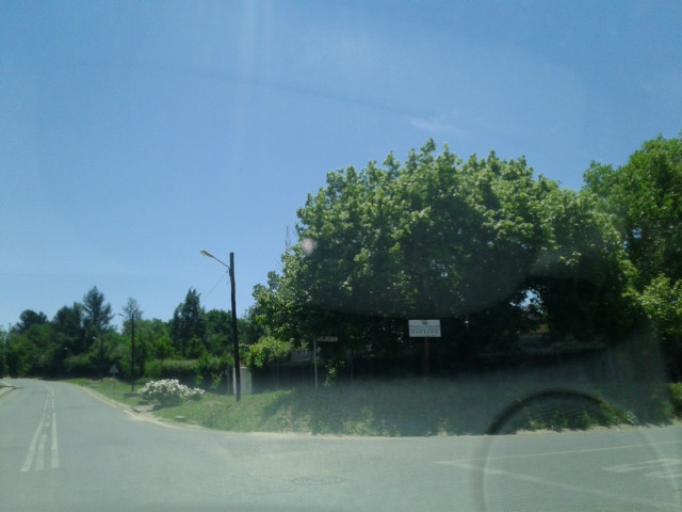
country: LS
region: Maseru
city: Maseru
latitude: -29.3082
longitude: 27.4783
